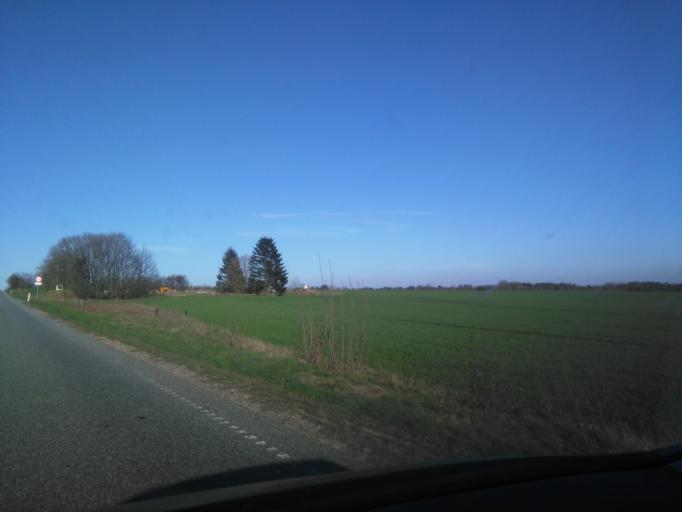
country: DK
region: Central Jutland
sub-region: Herning Kommune
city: Vildbjerg
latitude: 56.1080
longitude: 8.7420
